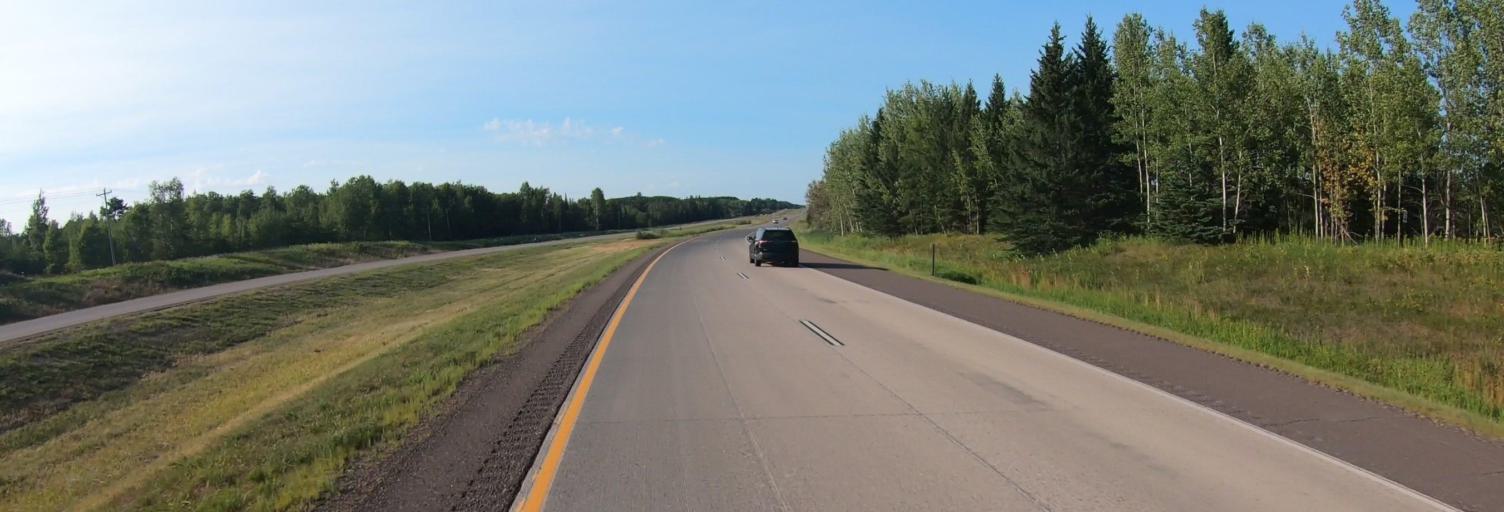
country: US
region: Minnesota
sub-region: Carlton County
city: Cloquet
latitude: 46.9773
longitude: -92.4694
